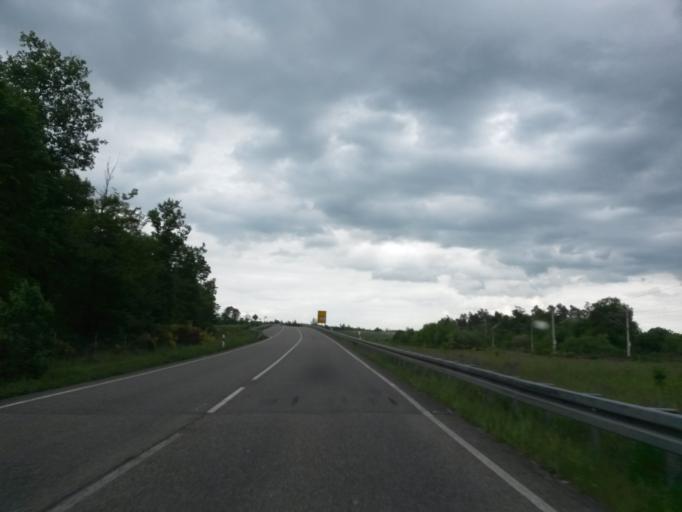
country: DE
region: Baden-Wuerttemberg
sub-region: Karlsruhe Region
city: Hambrucken
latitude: 49.2045
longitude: 8.5050
